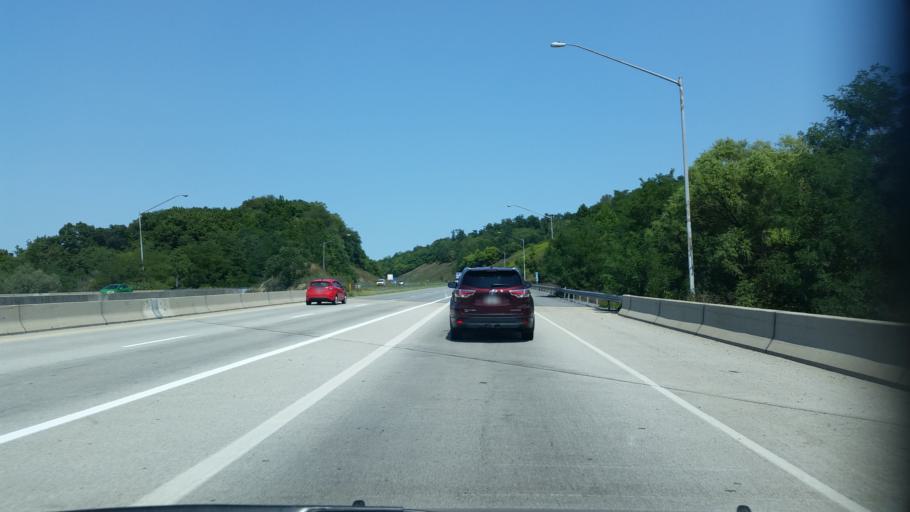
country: US
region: Pennsylvania
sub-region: Blair County
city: Duncansville
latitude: 40.4434
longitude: -78.4245
